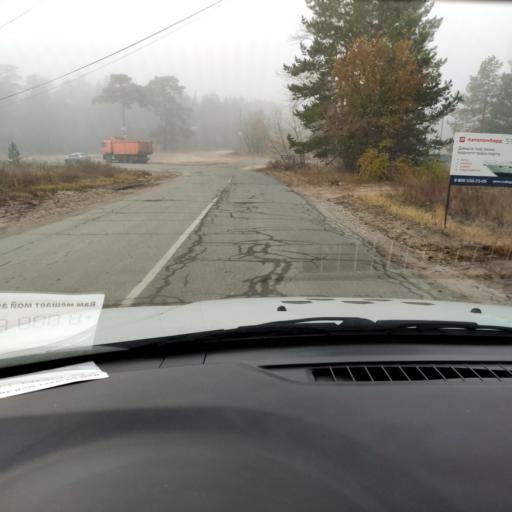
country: RU
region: Samara
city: Tol'yatti
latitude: 53.4709
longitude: 49.3720
